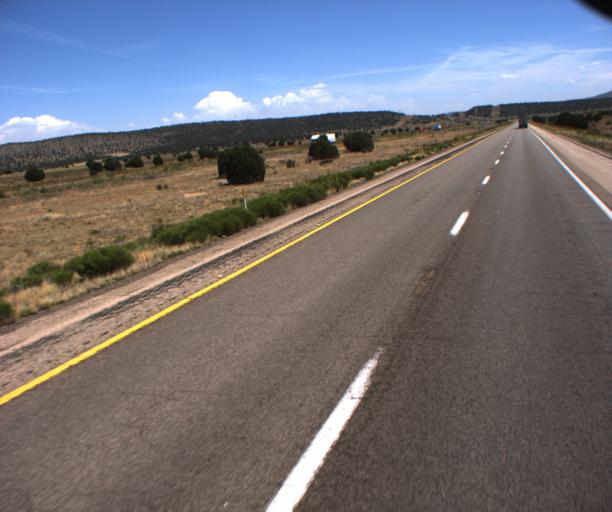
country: US
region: Arizona
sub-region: Mohave County
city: Peach Springs
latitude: 35.2286
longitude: -113.2273
